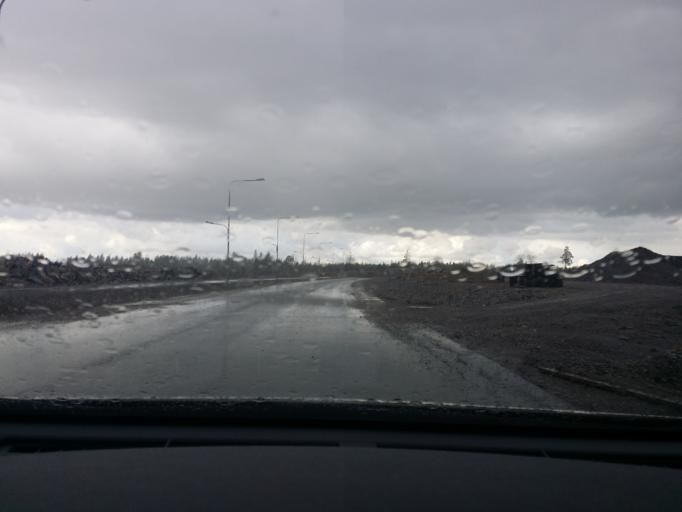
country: SE
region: Soedermanland
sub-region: Eskilstuna Kommun
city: Arla
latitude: 59.3624
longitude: 16.7001
